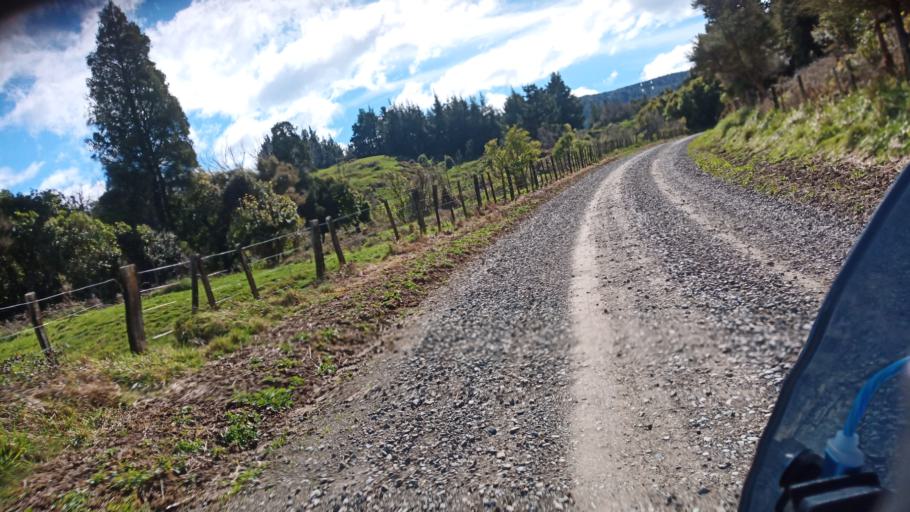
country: NZ
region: Hawke's Bay
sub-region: Wairoa District
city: Wairoa
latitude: -38.8176
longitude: 177.1568
